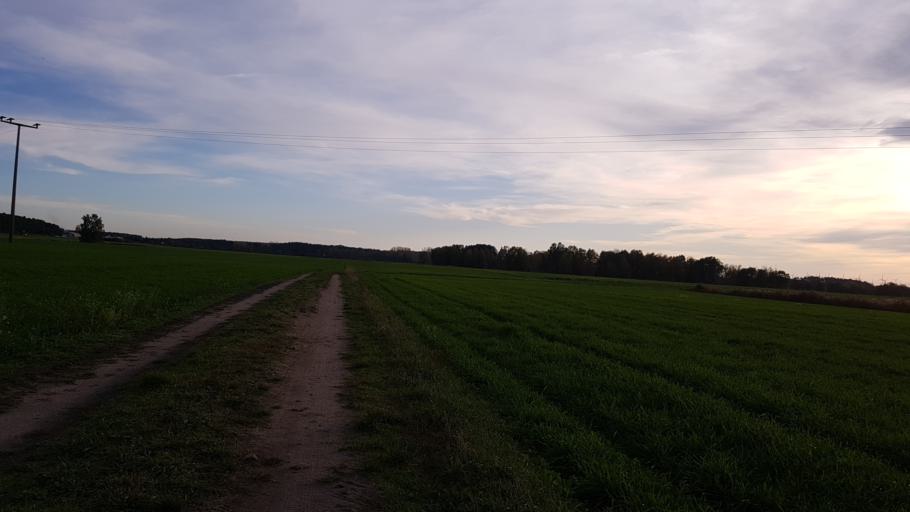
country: DE
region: Brandenburg
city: Trobitz
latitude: 51.5715
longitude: 13.4104
